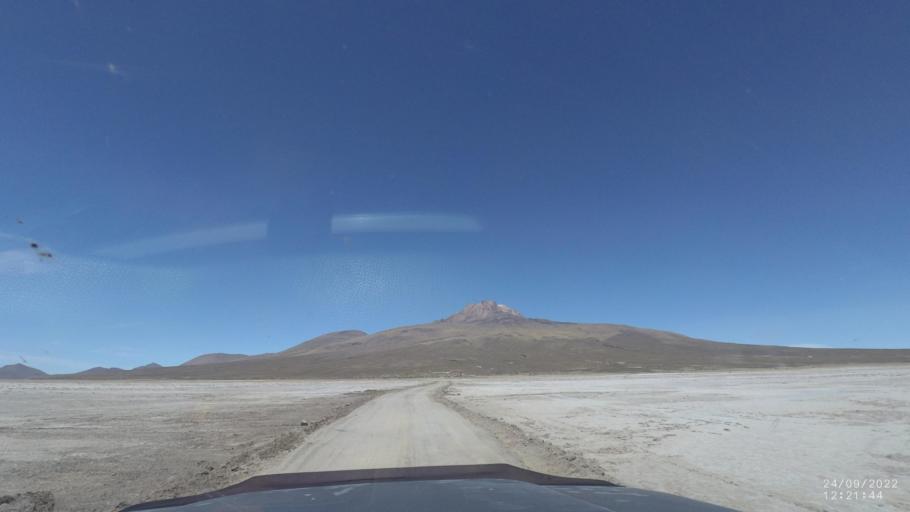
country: BO
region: Potosi
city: Colchani
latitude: -19.7508
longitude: -67.6678
